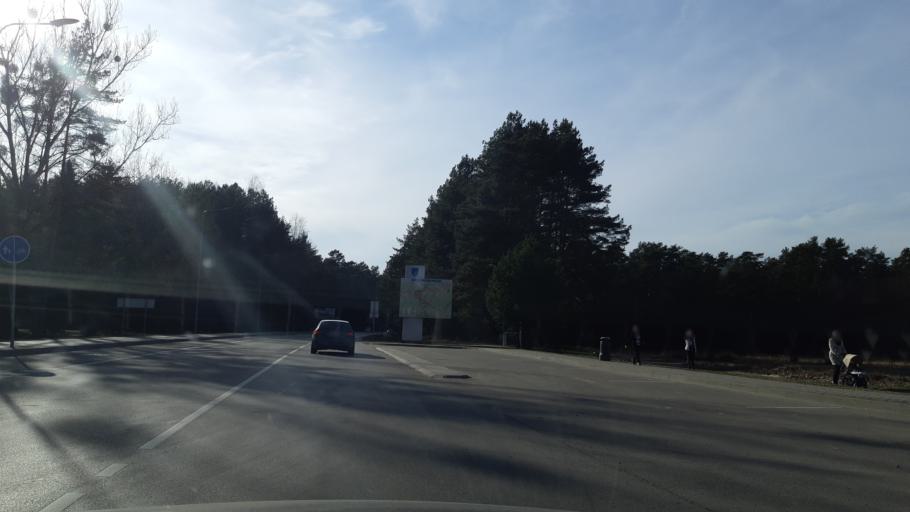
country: LT
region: Alytaus apskritis
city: Druskininkai
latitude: 54.0048
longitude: 24.0146
